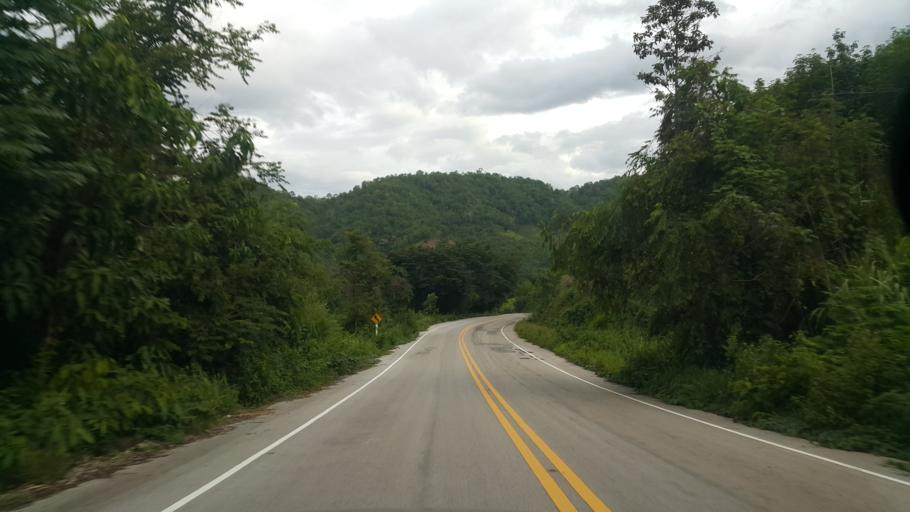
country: TH
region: Loei
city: Na Haeo
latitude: 17.4987
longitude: 101.0931
